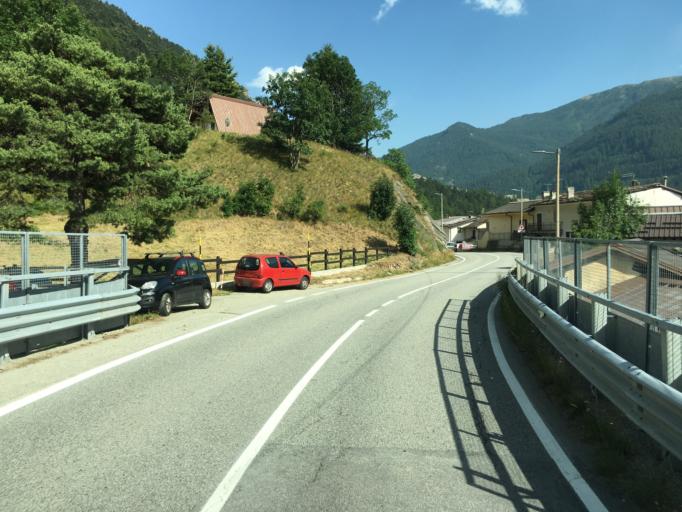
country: IT
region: Piedmont
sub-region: Provincia di Torino
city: Fenestrelle
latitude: 45.0352
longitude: 7.0531
